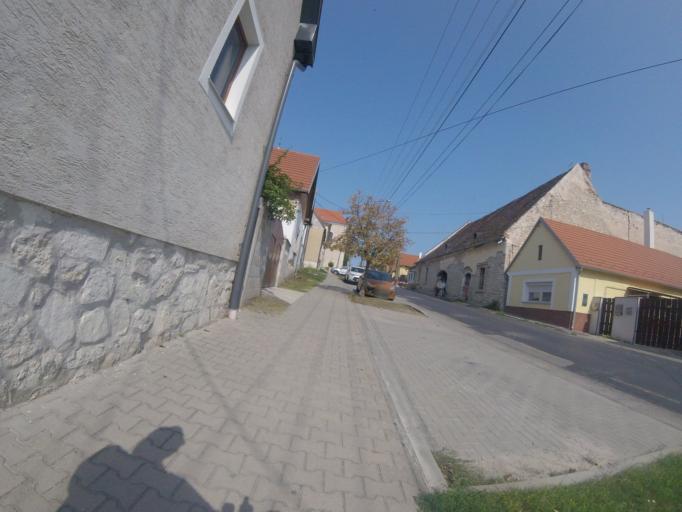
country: HU
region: Gyor-Moson-Sopron
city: Fertorakos
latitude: 47.7184
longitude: 16.6521
